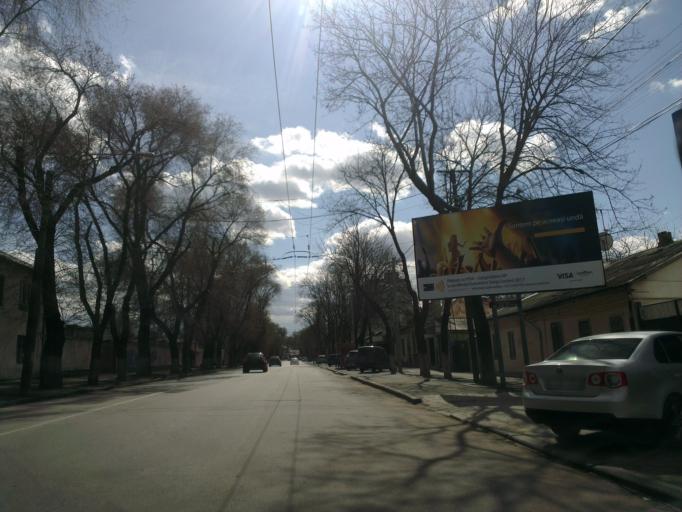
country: MD
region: Chisinau
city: Chisinau
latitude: 47.0123
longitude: 28.8280
